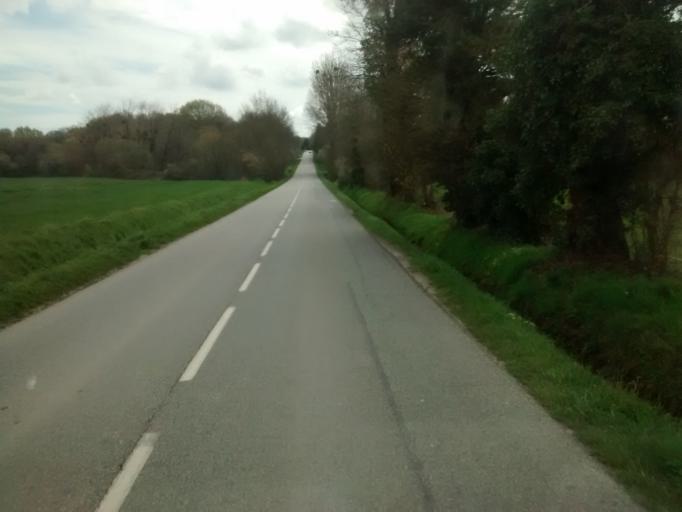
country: FR
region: Brittany
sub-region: Departement du Morbihan
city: Ploermel
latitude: 47.9049
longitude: -2.3789
